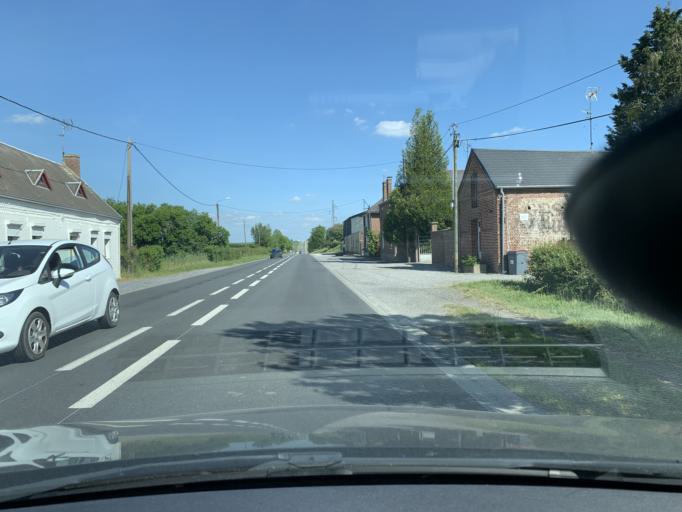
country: FR
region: Nord-Pas-de-Calais
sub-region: Departement du Nord
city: Viesly
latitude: 50.1206
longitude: 3.4698
